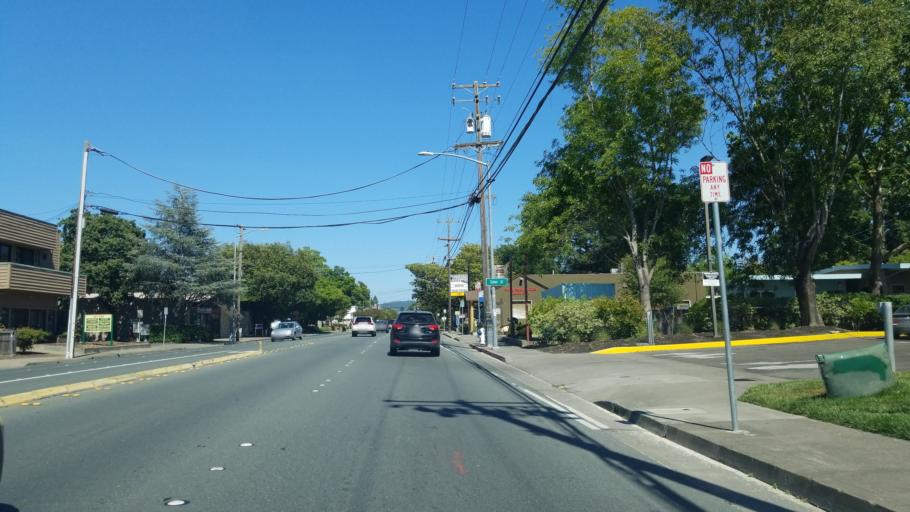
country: US
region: California
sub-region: Sonoma County
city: Santa Rosa
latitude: 38.4456
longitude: -122.7174
